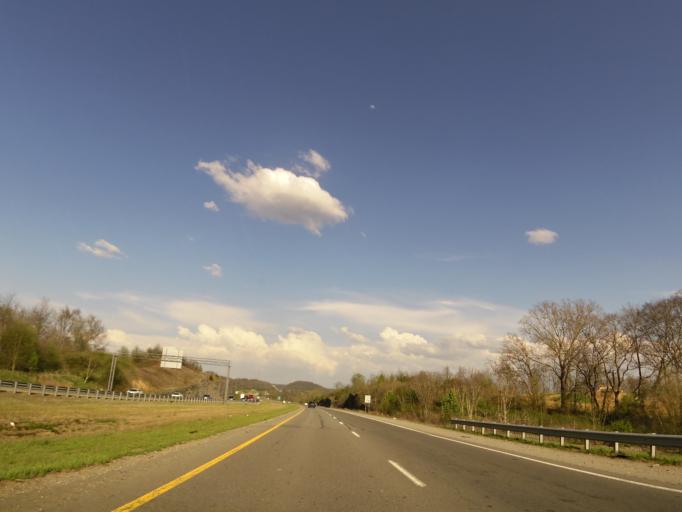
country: US
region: Tennessee
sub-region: Williamson County
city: Thompson's Station
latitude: 35.8208
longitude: -86.8750
